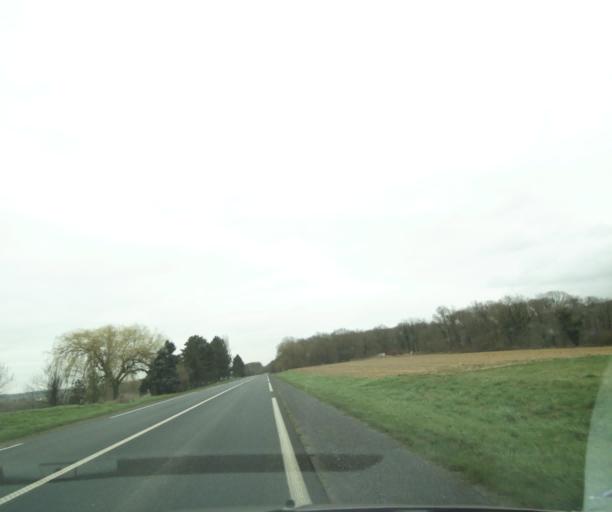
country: FR
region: Picardie
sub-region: Departement de l'Oise
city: Crisolles
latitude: 49.6077
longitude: 3.0174
